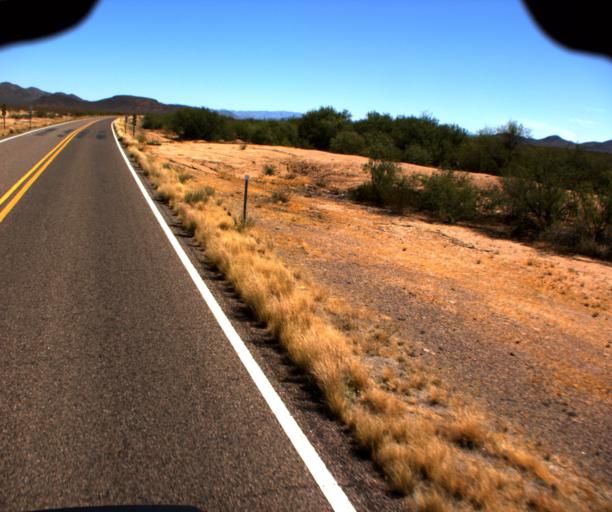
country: US
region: Arizona
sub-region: Yavapai County
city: Congress
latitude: 33.9870
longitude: -113.1361
